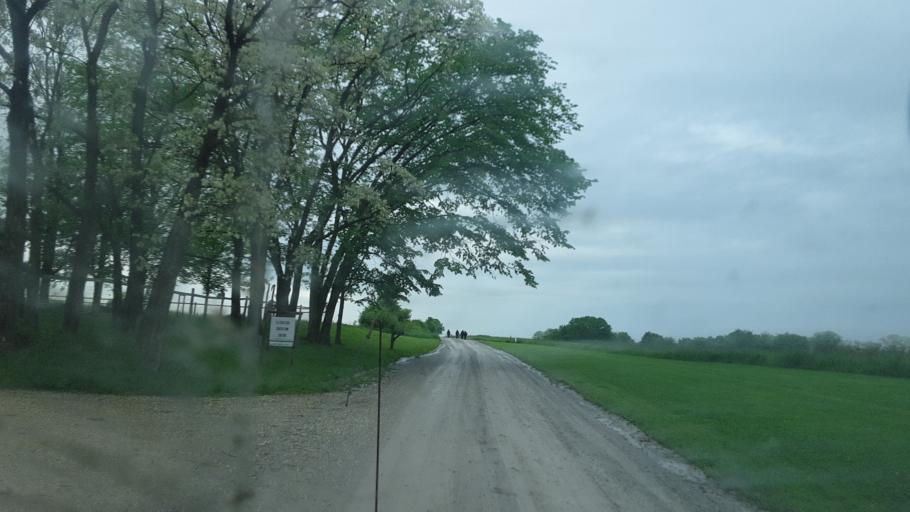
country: US
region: Missouri
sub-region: Clark County
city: Kahoka
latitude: 40.4370
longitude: -91.6157
